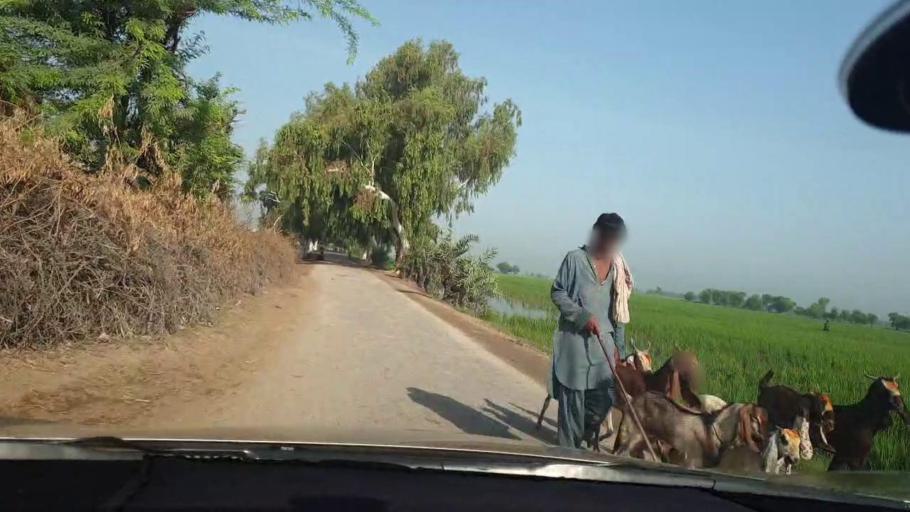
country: PK
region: Sindh
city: Kambar
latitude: 27.6507
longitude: 68.0402
